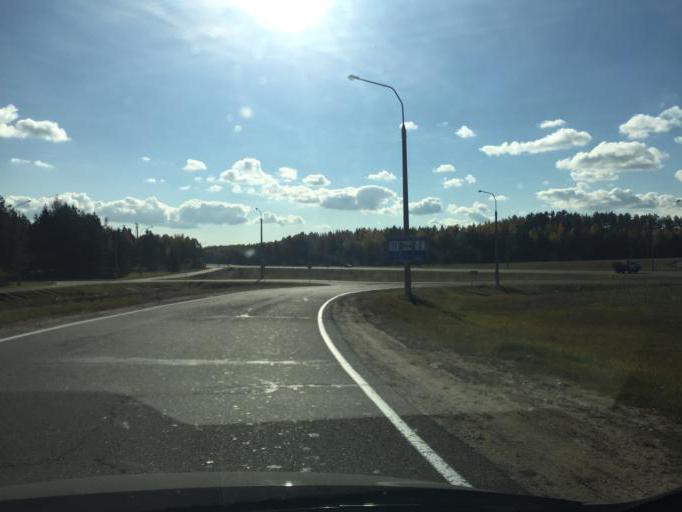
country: BY
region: Minsk
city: Slabada
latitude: 53.9490
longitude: 27.9797
